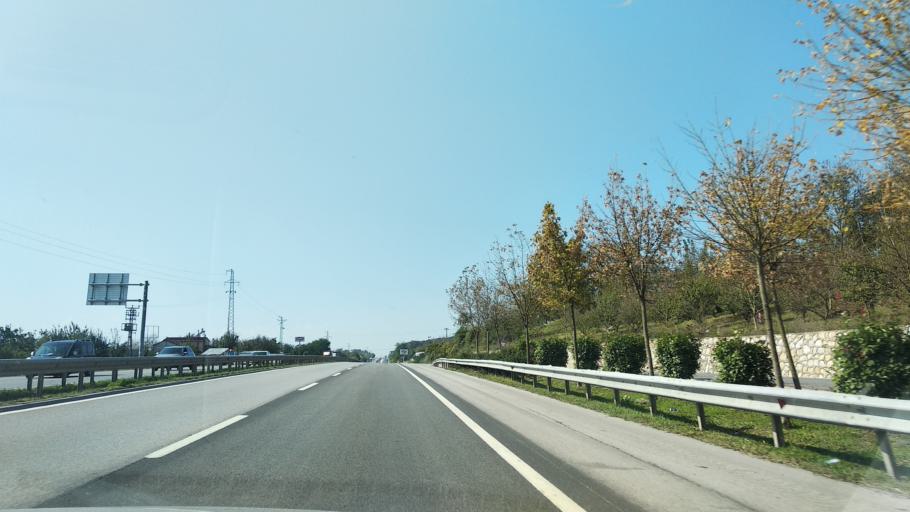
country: TR
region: Kocaeli
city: Derbent
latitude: 40.7319
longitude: 30.1786
